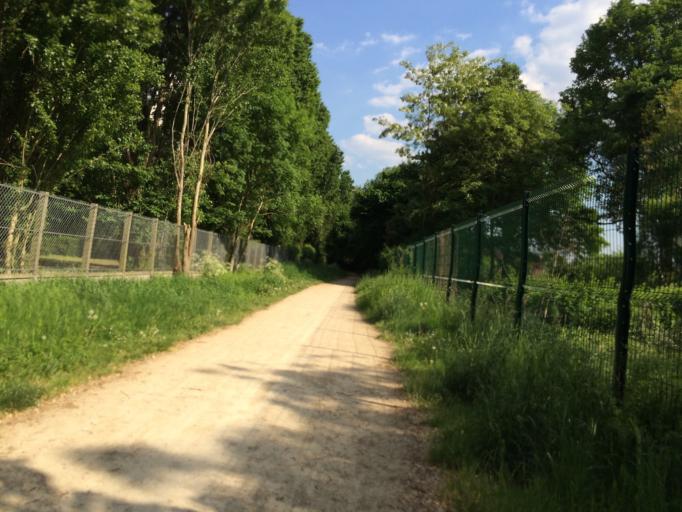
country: FR
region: Ile-de-France
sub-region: Departement de l'Essonne
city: Grigny
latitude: 48.6455
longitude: 2.3993
